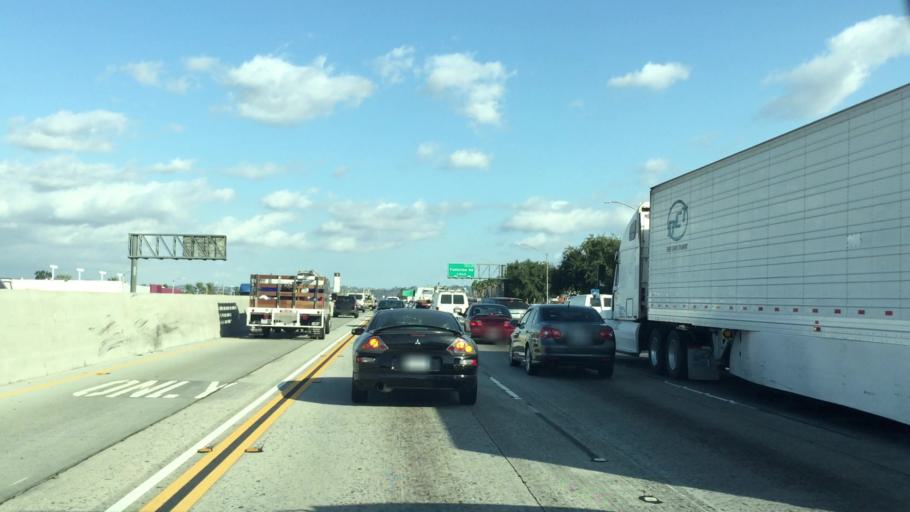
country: US
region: California
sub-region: Los Angeles County
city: South San Jose Hills
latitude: 33.9965
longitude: -117.9279
